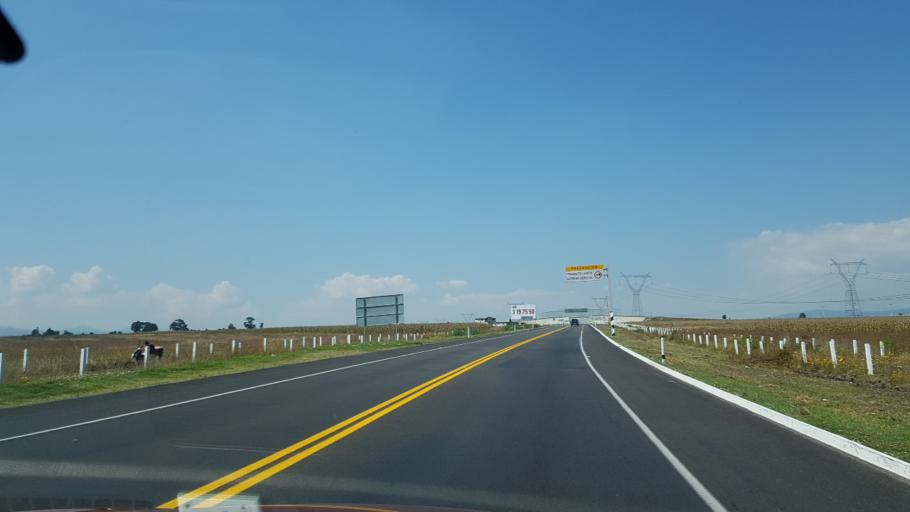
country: MX
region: Mexico
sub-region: Toluca
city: Sebastian Lerdo de Tejada
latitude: 19.3868
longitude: -99.7144
